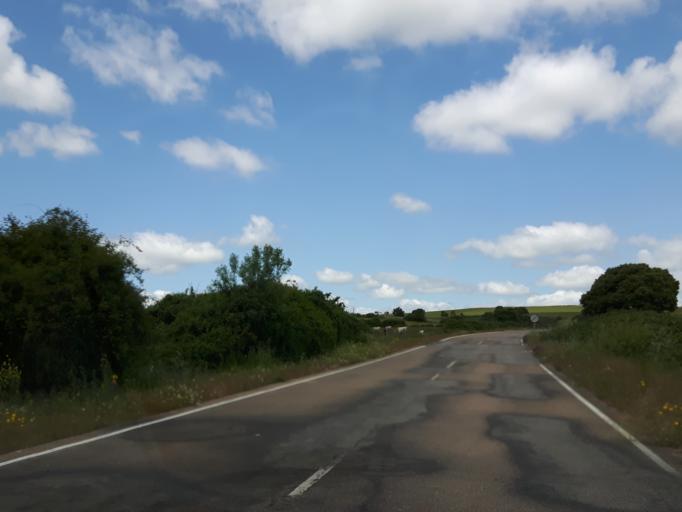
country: ES
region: Castille and Leon
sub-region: Provincia de Salamanca
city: Villar de la Yegua
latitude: 40.7158
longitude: -6.6914
